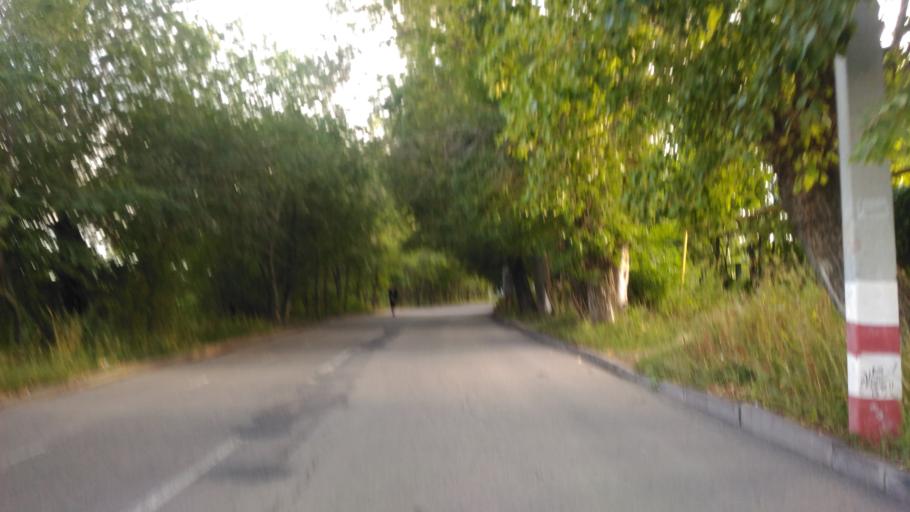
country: RU
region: Ulyanovsk
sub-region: Ulyanovskiy Rayon
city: Ulyanovsk
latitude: 54.3231
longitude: 48.4098
